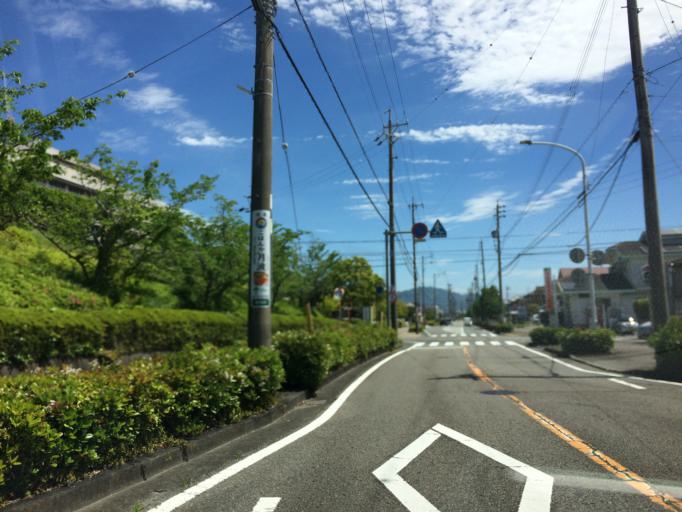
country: JP
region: Shizuoka
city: Fujieda
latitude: 34.8597
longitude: 138.2294
